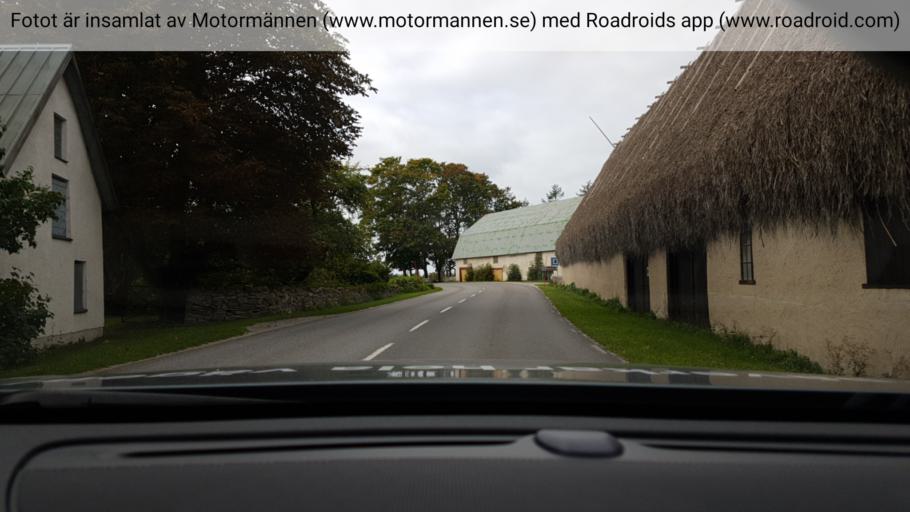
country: SE
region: Gotland
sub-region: Gotland
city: Hemse
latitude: 56.9919
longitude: 18.2473
